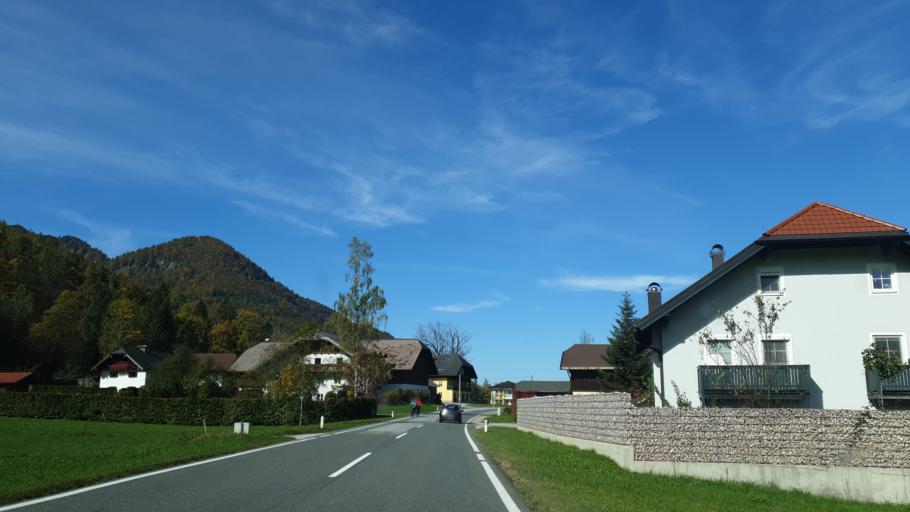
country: AT
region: Salzburg
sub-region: Politischer Bezirk Salzburg-Umgebung
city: Hintersee
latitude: 47.7303
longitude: 13.2682
